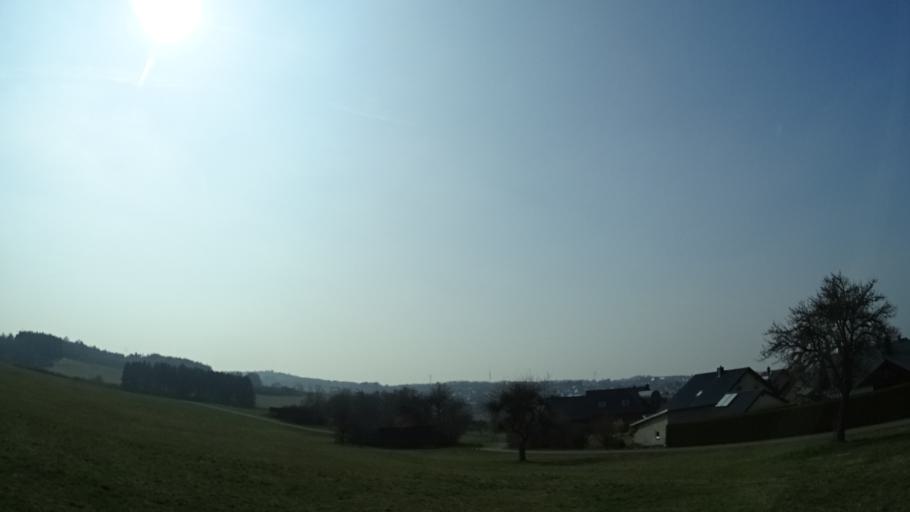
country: DE
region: Rheinland-Pfalz
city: Baumholder
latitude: 49.6092
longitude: 7.3459
